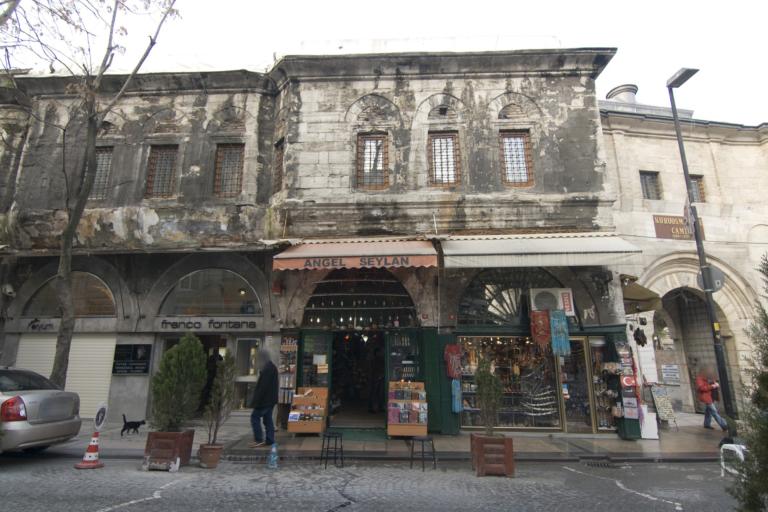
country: TR
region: Istanbul
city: Eminoenue
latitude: 41.0100
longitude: 28.9712
